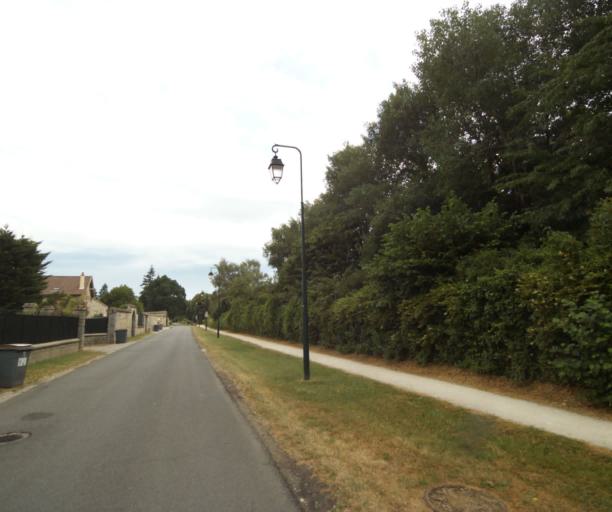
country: FR
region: Ile-de-France
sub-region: Departement de Seine-et-Marne
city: Cely
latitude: 48.4479
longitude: 2.5510
